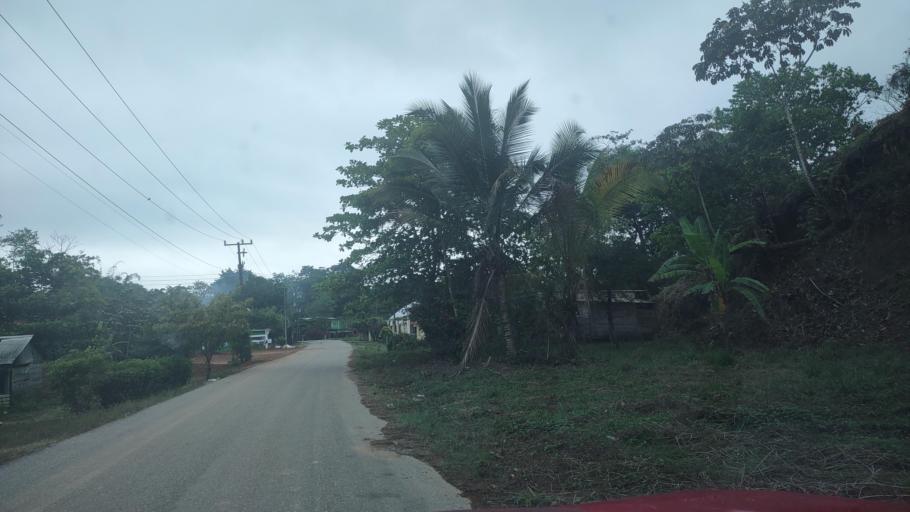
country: MX
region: Veracruz
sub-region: Uxpanapa
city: Poblado 10
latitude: 17.4754
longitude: -94.1200
